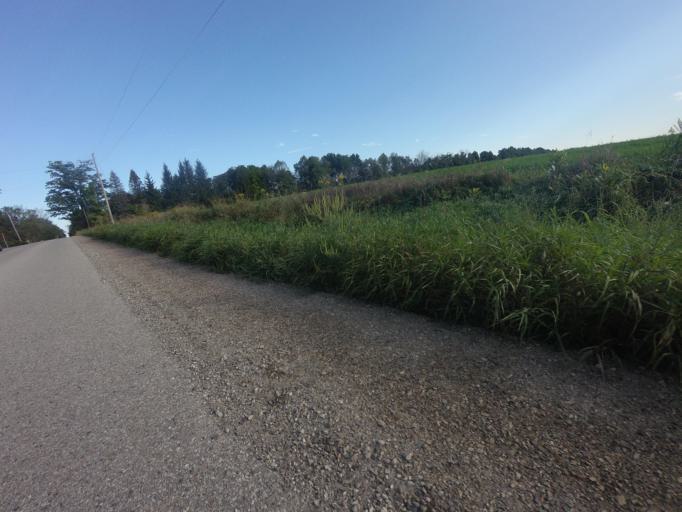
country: CA
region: Ontario
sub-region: Wellington County
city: Guelph
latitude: 43.6123
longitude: -80.3627
